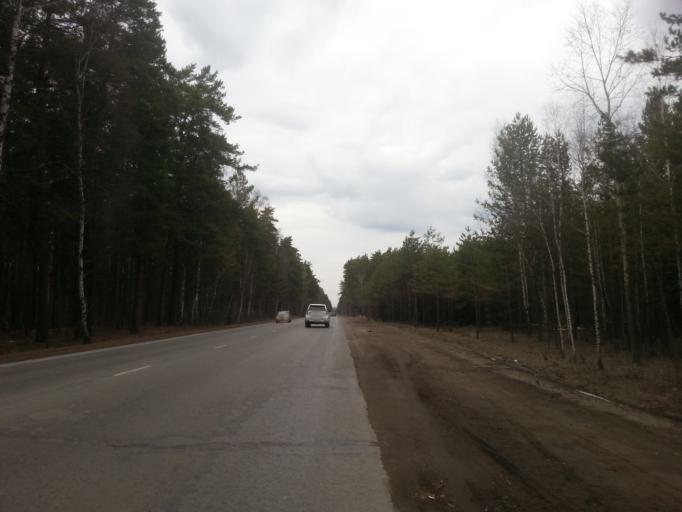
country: RU
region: Altai Krai
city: Yuzhnyy
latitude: 53.2734
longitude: 83.7225
